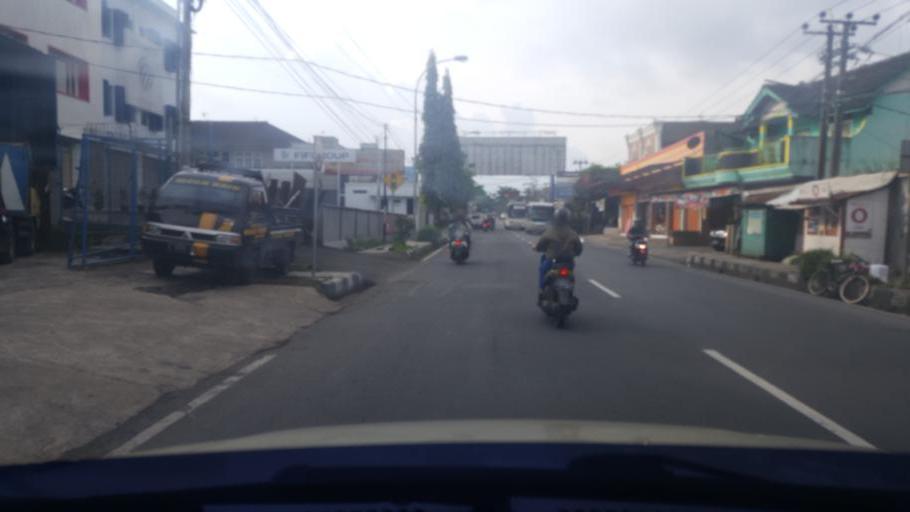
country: ID
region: West Java
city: Jati
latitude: -7.3054
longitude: 108.2065
